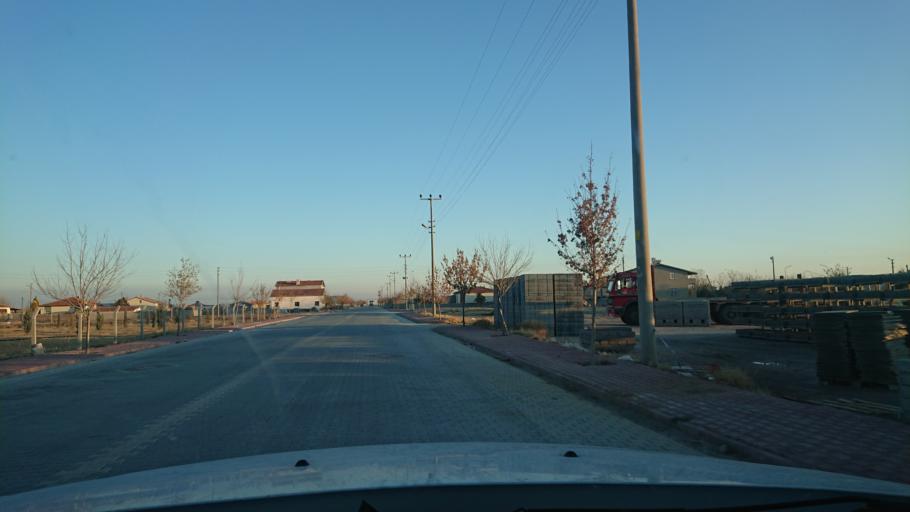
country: TR
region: Aksaray
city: Eskil
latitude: 38.3976
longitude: 33.4209
